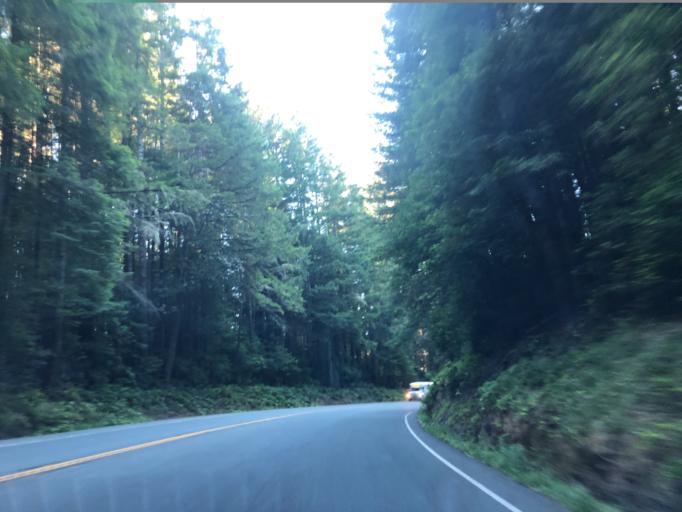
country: US
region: California
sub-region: Del Norte County
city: Bertsch-Oceanview
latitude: 41.6859
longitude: -124.1069
